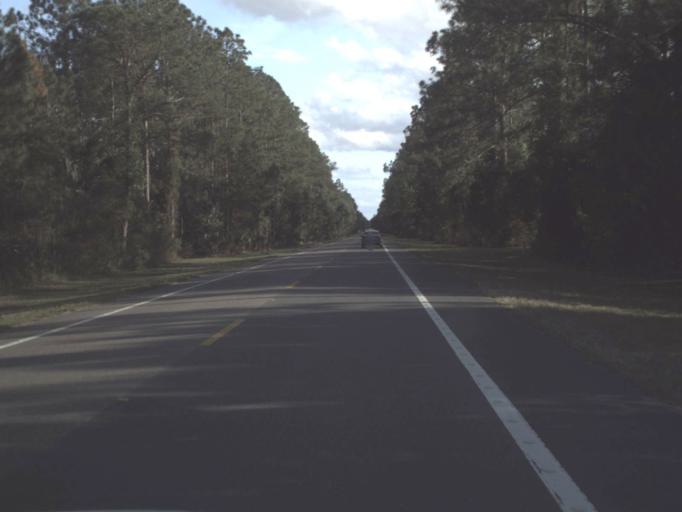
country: US
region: Florida
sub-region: Flagler County
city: Bunnell
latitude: 29.3688
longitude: -81.3118
